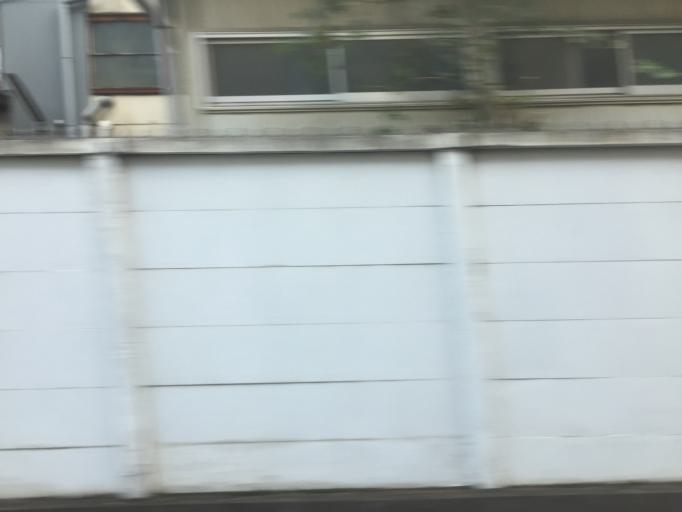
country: JP
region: Kanagawa
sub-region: Kawasaki-shi
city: Kawasaki
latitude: 35.5662
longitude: 139.6845
